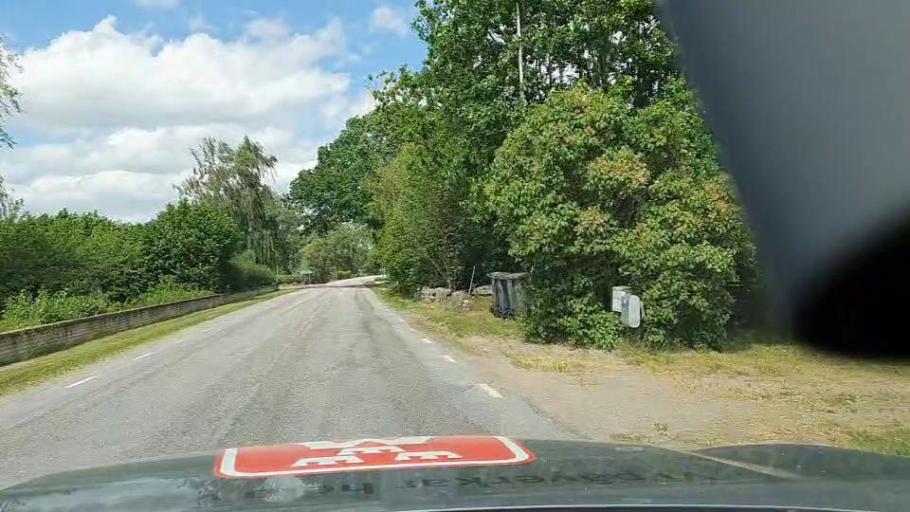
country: SE
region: Blekinge
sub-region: Karlshamns Kommun
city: Morrum
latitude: 56.1050
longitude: 14.6849
